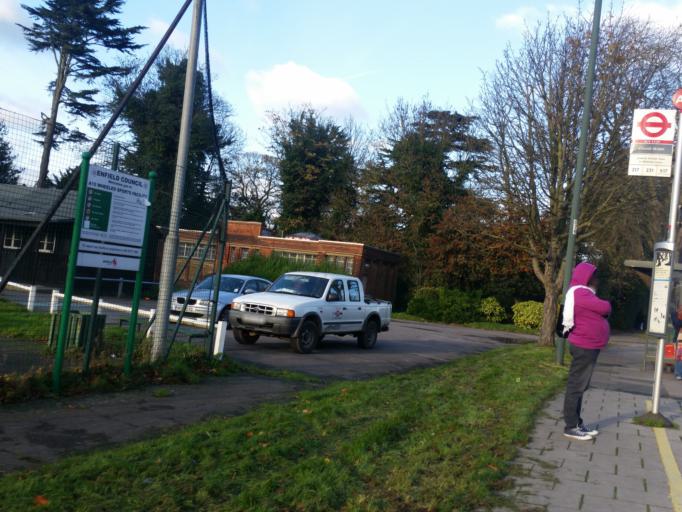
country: GB
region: England
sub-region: Greater London
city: Enfield
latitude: 51.6291
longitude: -0.0790
